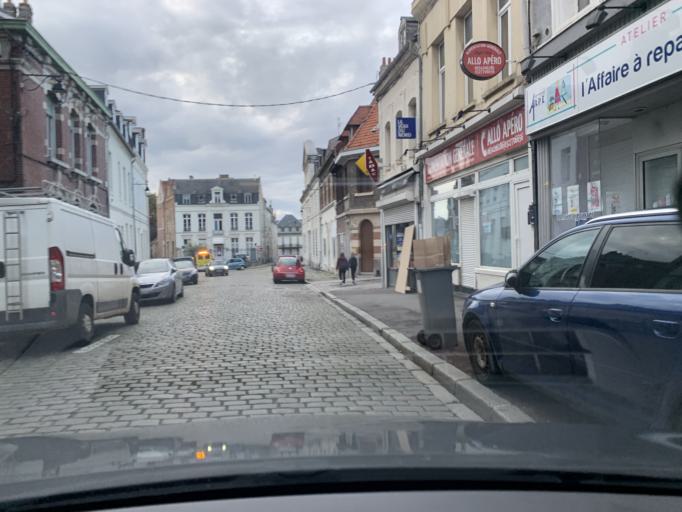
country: FR
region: Nord-Pas-de-Calais
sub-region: Departement du Nord
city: Cambrai
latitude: 50.1772
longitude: 3.2318
